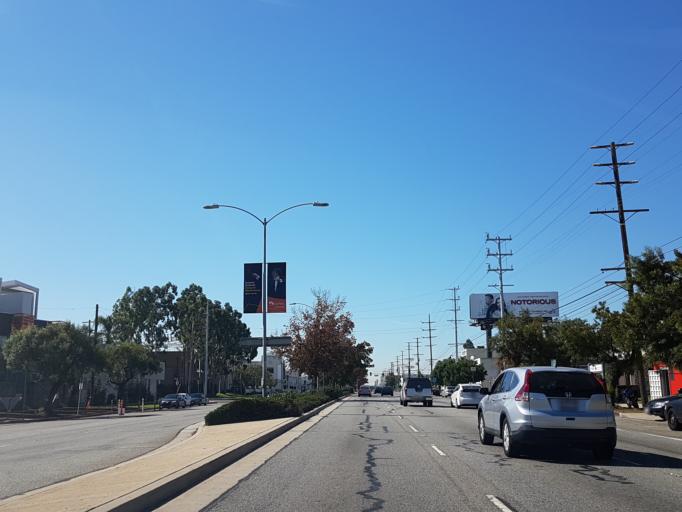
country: US
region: California
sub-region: Los Angeles County
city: Culver City
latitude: 34.0325
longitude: -118.3829
